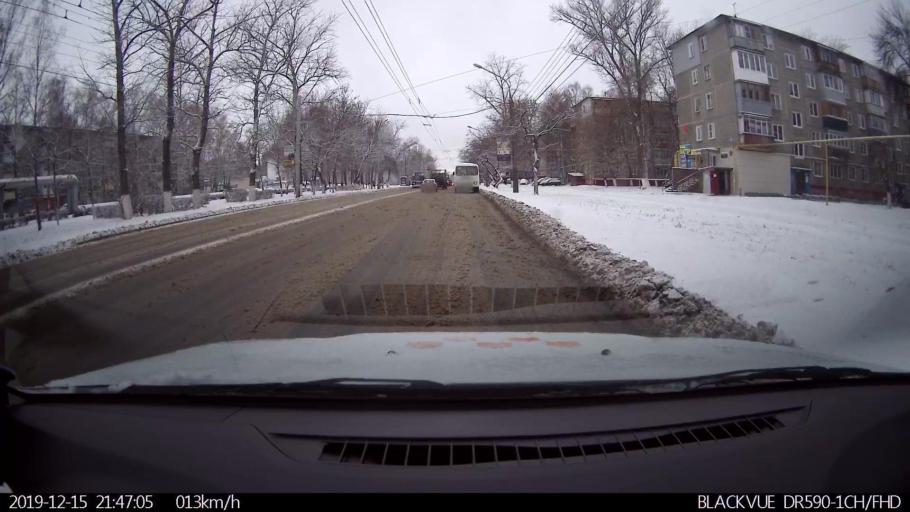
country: RU
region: Nizjnij Novgorod
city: Burevestnik
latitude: 56.2310
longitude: 43.8738
